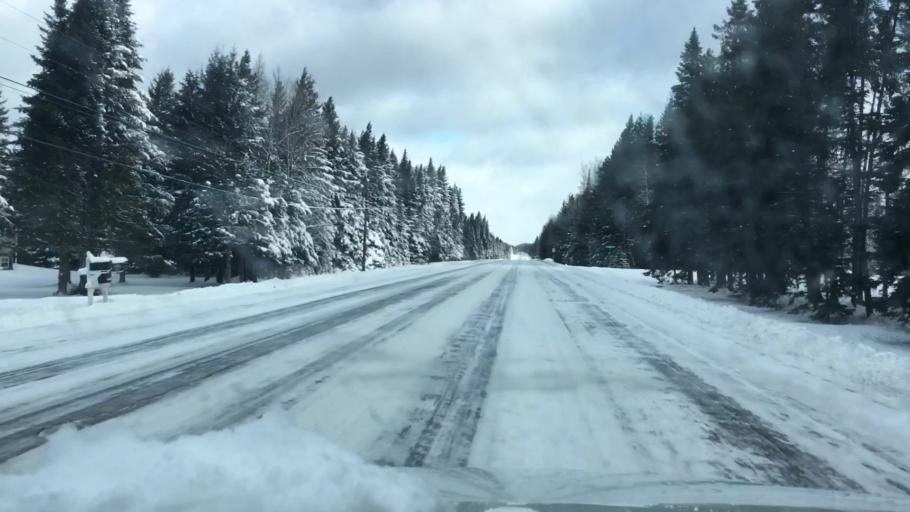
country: US
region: Maine
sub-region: Aroostook County
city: Madawaska
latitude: 47.0139
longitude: -68.0178
